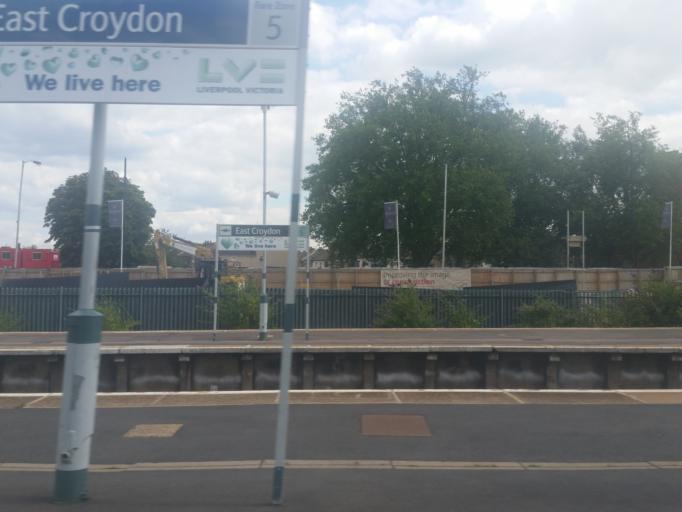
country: GB
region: England
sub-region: Greater London
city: Croydon
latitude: 51.3774
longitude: -0.0922
